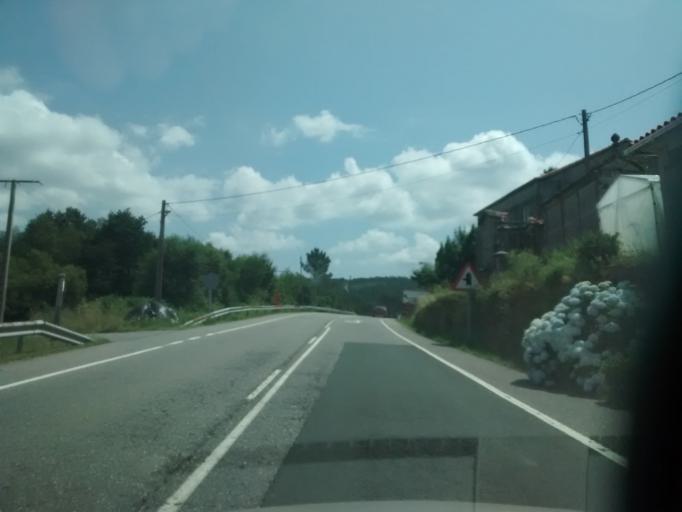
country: ES
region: Galicia
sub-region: Provincia de Pontevedra
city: Forcarei
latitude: 42.5436
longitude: -8.3518
